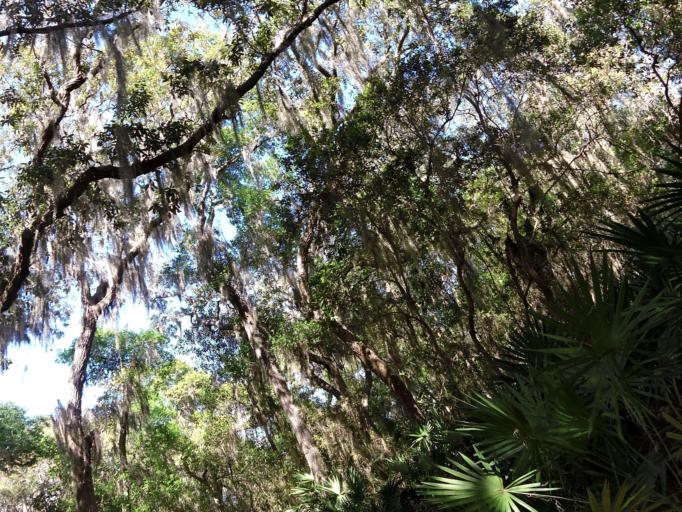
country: US
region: Florida
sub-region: Duval County
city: Atlantic Beach
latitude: 30.4549
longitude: -81.4804
